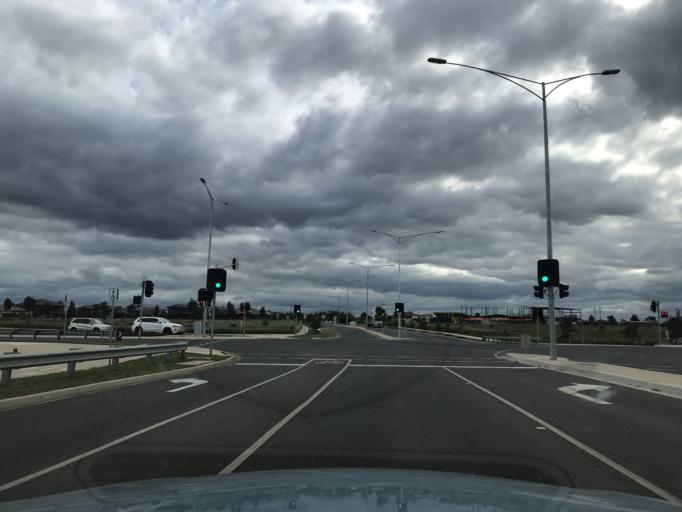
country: AU
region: Victoria
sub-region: Wyndham
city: Williams Landing
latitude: -37.8434
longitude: 144.7323
